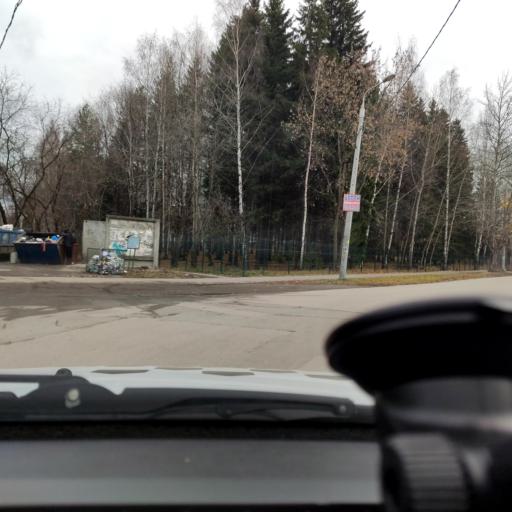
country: RU
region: Perm
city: Kondratovo
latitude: 58.0449
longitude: 56.1014
